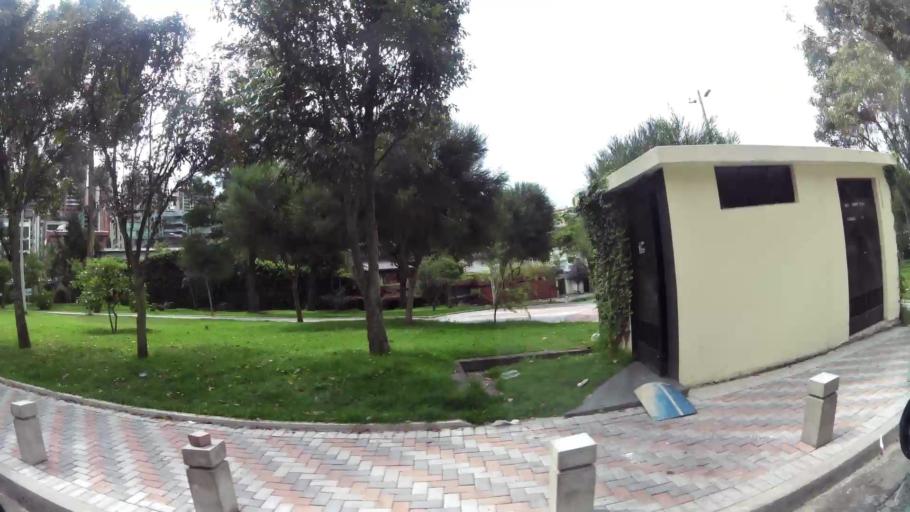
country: EC
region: Pichincha
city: Quito
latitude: -0.1692
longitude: -78.4955
